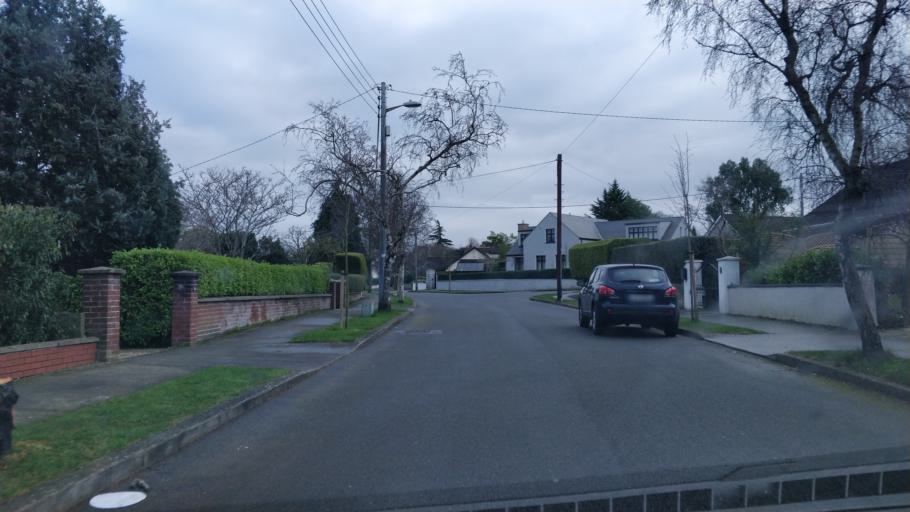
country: IE
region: Leinster
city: Foxrock
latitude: 53.2808
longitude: -6.1785
